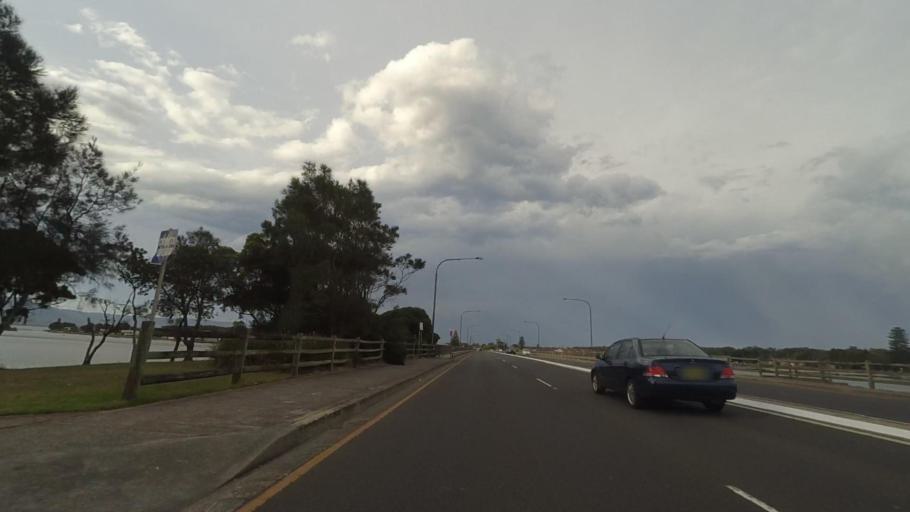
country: AU
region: New South Wales
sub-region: Shellharbour
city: Lake Illawarra
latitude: -34.5376
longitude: 150.8662
